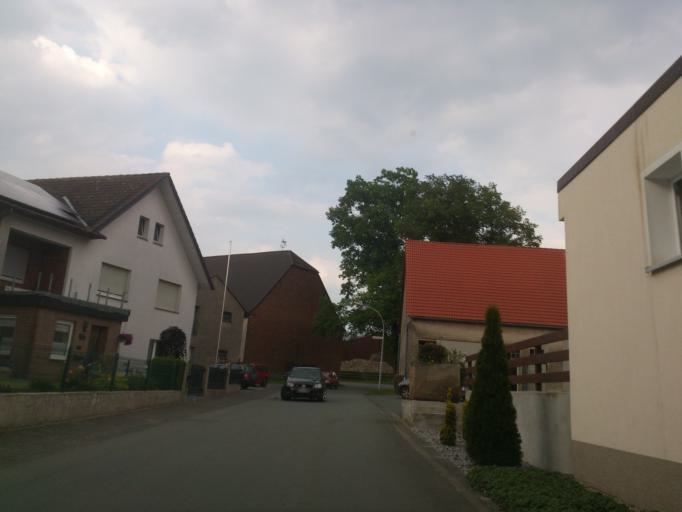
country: DE
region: North Rhine-Westphalia
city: Lichtenau
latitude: 51.6653
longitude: 8.8381
